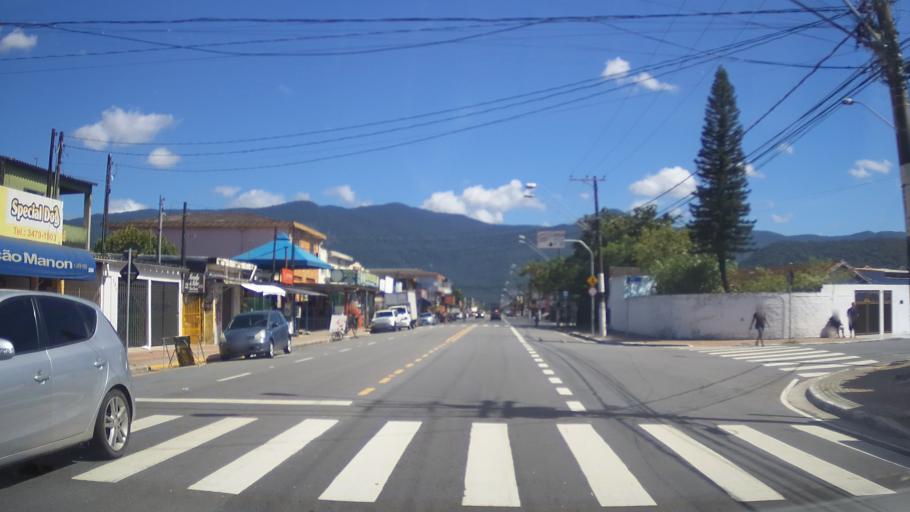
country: BR
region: Sao Paulo
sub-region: Mongagua
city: Mongagua
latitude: -24.0359
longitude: -46.5271
